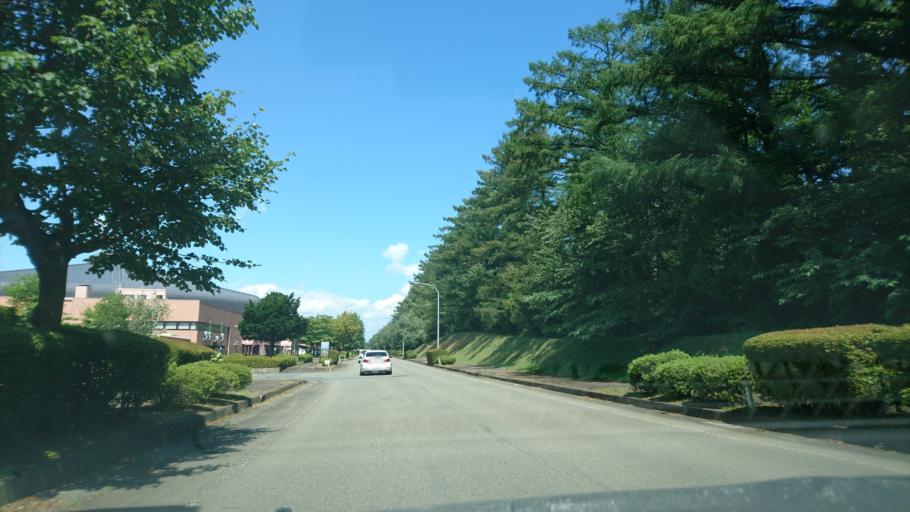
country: JP
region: Iwate
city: Morioka-shi
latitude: 39.8071
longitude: 141.1324
